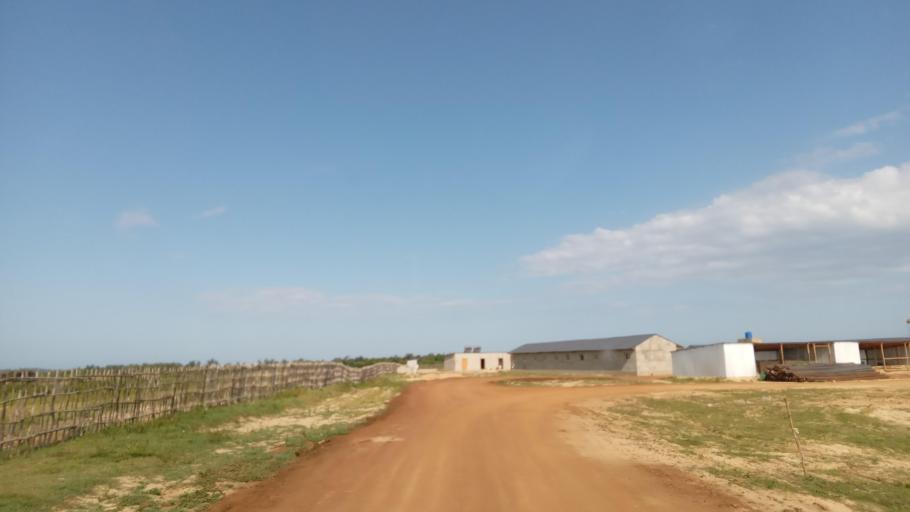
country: MG
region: Atsimo-Atsinanana
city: Vohipaho
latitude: -23.8116
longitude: 47.5491
